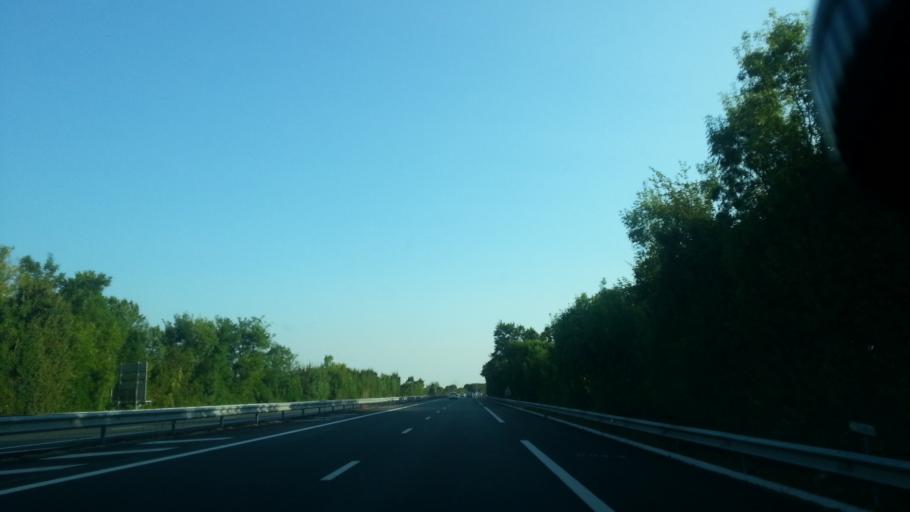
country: FR
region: Poitou-Charentes
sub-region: Departement des Deux-Sevres
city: Beauvoir-sur-Niort
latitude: 46.1290
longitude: -0.5305
